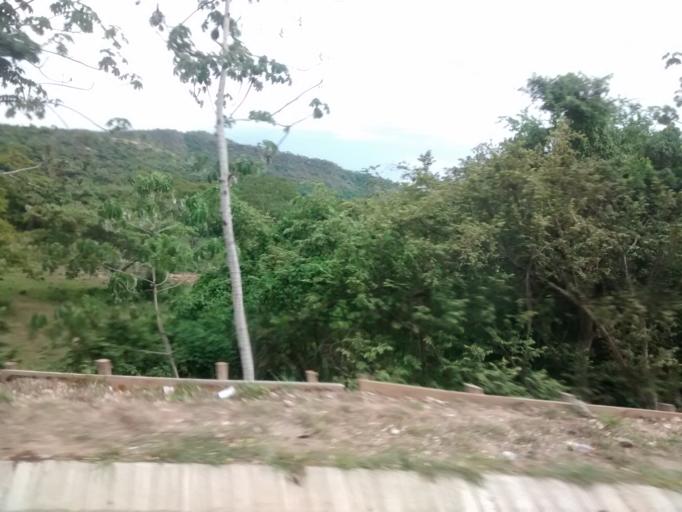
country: CO
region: Cundinamarca
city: Ricaurte
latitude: 4.2445
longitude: -74.7429
